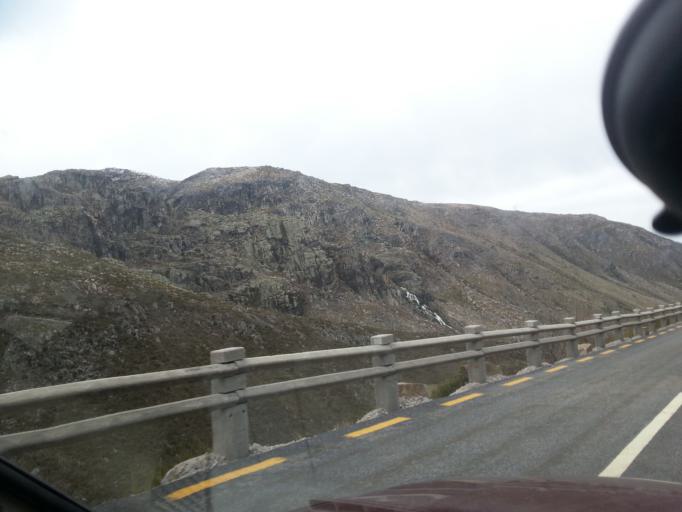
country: PT
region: Guarda
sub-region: Manteigas
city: Manteigas
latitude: 40.3354
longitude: -7.5691
